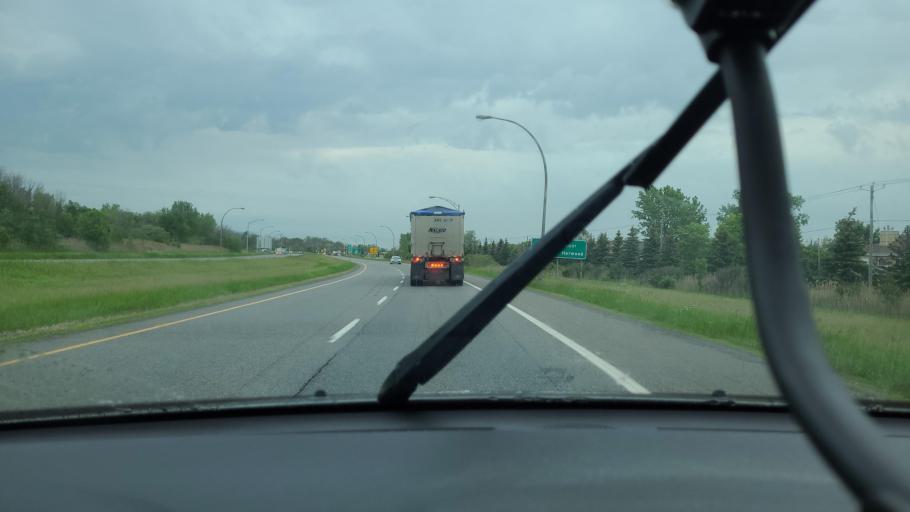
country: CA
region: Quebec
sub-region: Monteregie
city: Vaudreuil-Dorion
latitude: 45.3710
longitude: -74.0309
